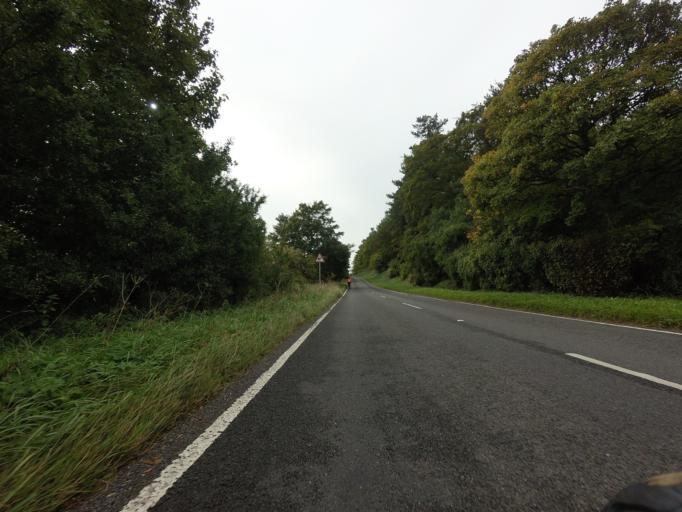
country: GB
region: England
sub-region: Hertfordshire
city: Reed
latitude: 52.0158
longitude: 0.0288
